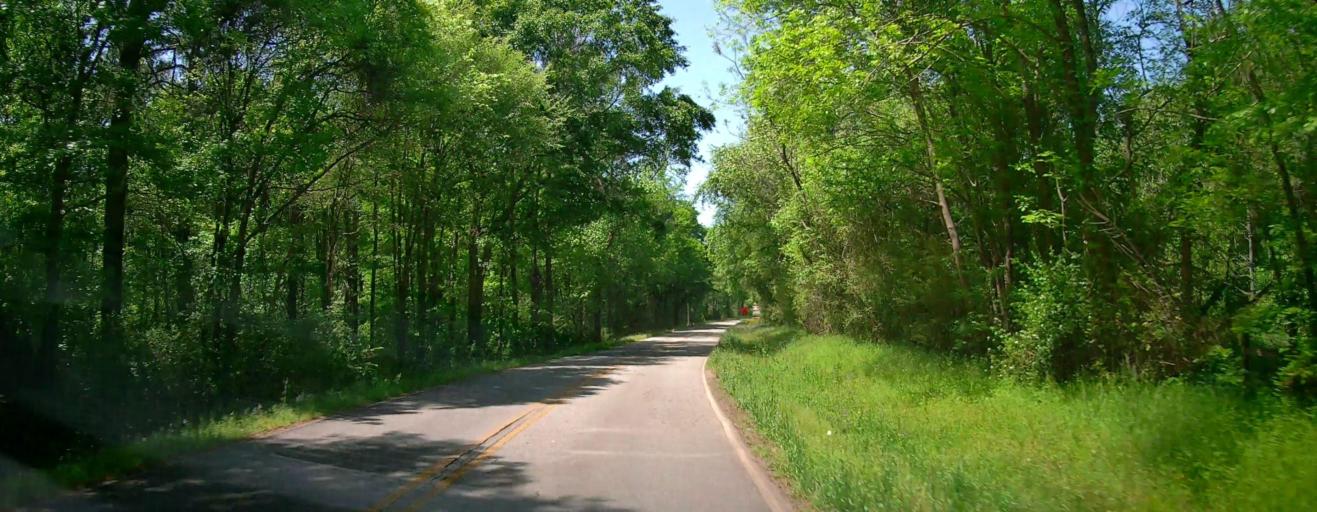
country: US
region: Georgia
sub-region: Jasper County
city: Monticello
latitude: 33.2814
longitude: -83.7106
